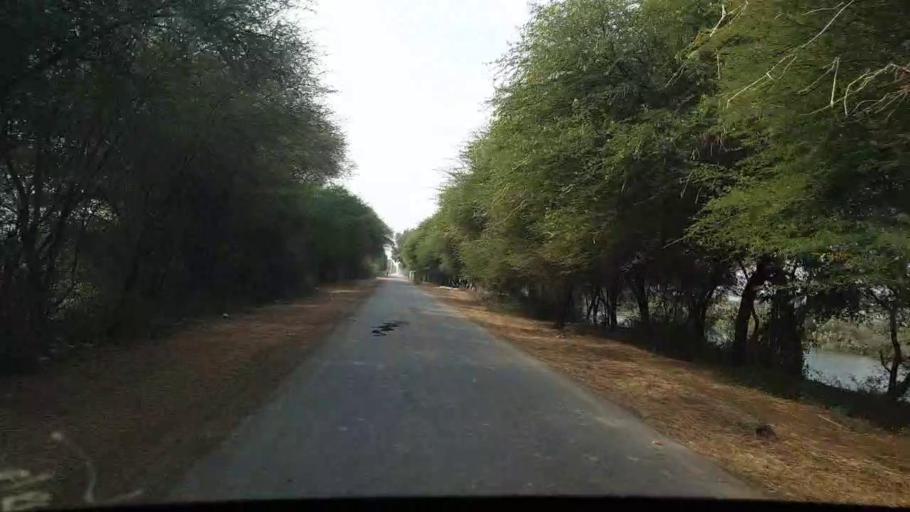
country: PK
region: Sindh
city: Chuhar Jamali
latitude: 24.3891
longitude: 67.9491
